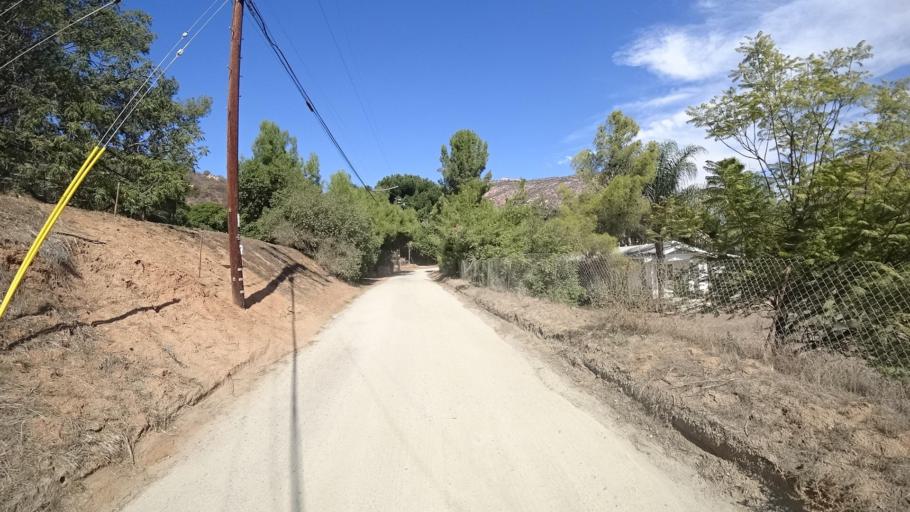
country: US
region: California
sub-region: San Diego County
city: Harbison Canyon
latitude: 32.8195
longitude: -116.8323
